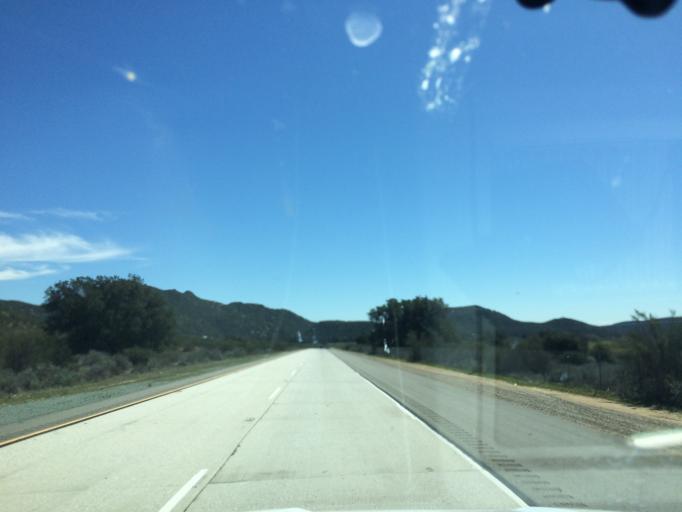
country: US
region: California
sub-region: San Diego County
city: Pine Valley
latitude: 32.7514
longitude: -116.4828
